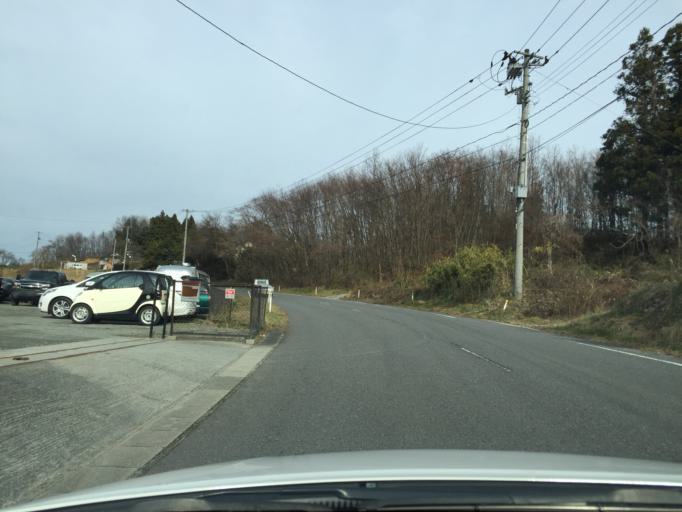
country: JP
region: Fukushima
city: Funehikimachi-funehiki
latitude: 37.3979
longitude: 140.5928
